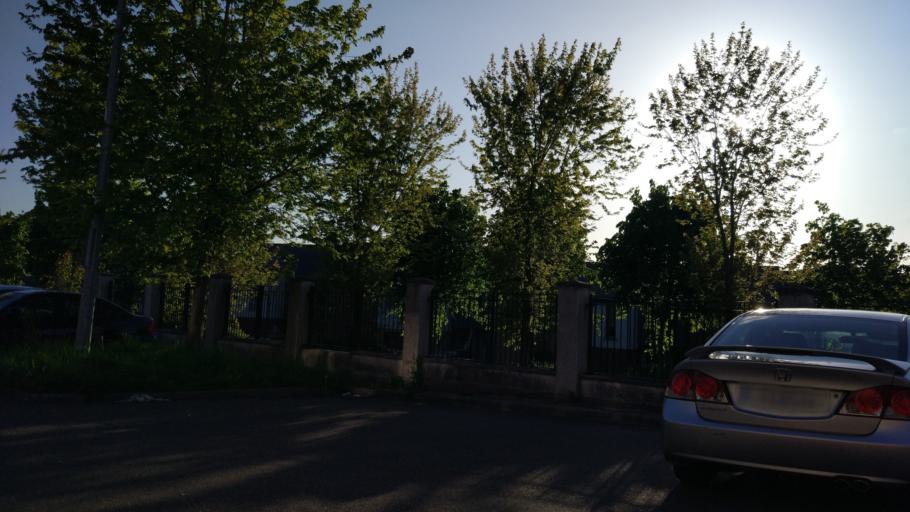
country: IE
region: Munster
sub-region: County Cork
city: Cork
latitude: 51.9098
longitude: -8.4666
